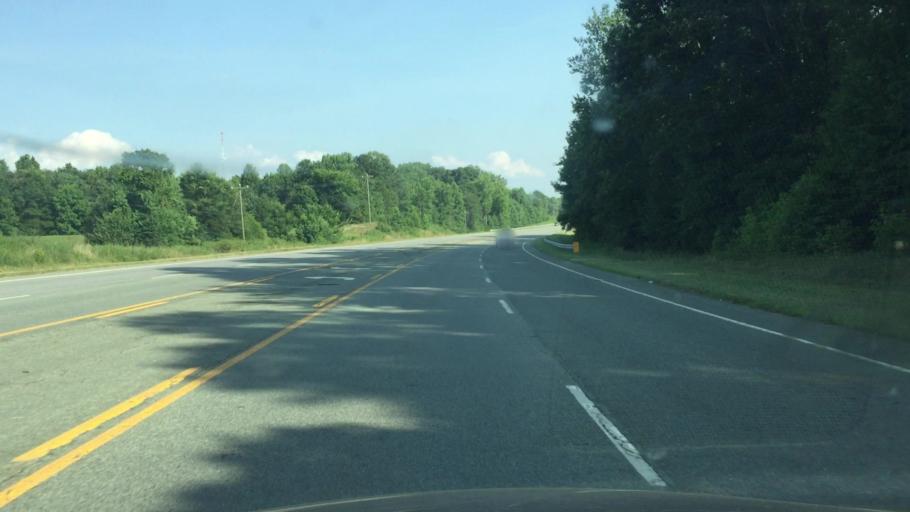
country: US
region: North Carolina
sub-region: Rockingham County
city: Reidsville
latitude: 36.3213
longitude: -79.6347
